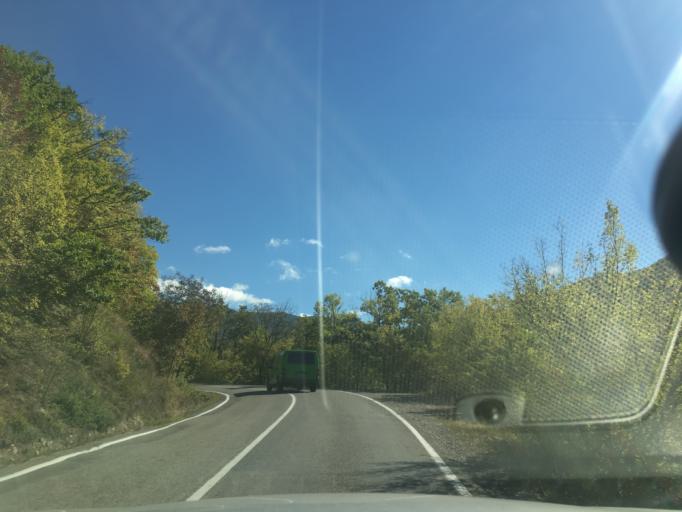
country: GE
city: Didi Lilo
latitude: 41.8618
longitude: 44.9079
